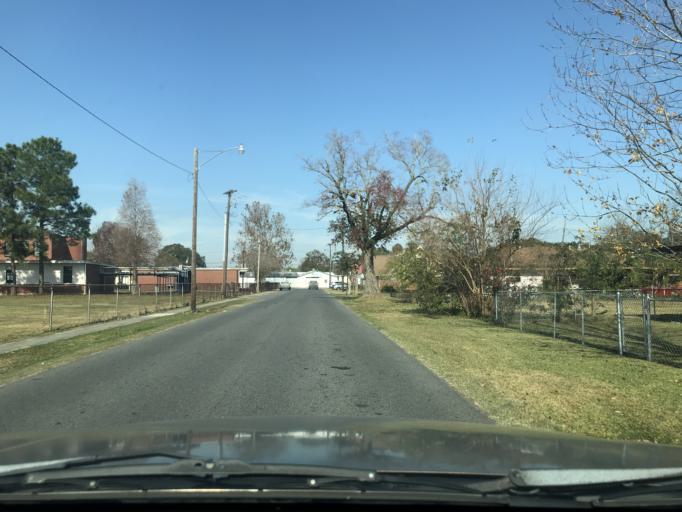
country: US
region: Louisiana
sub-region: Jefferson Parish
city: Marrero
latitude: 29.8988
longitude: -90.0903
